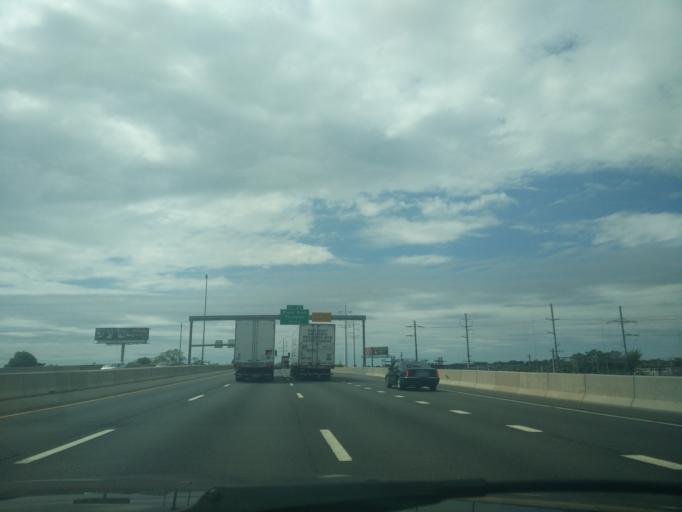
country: US
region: Connecticut
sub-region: Fairfield County
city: Bridgeport
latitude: 41.1668
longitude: -73.2157
